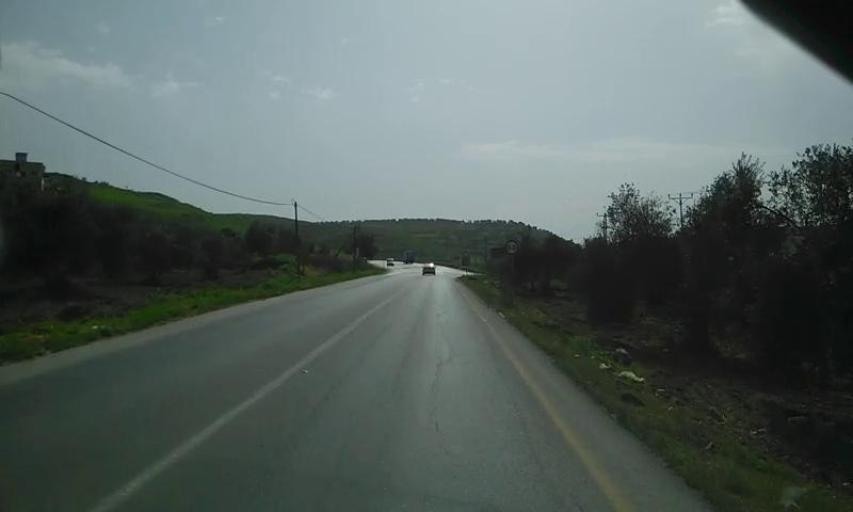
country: PS
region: West Bank
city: `Arrabah
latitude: 32.3885
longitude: 35.2162
